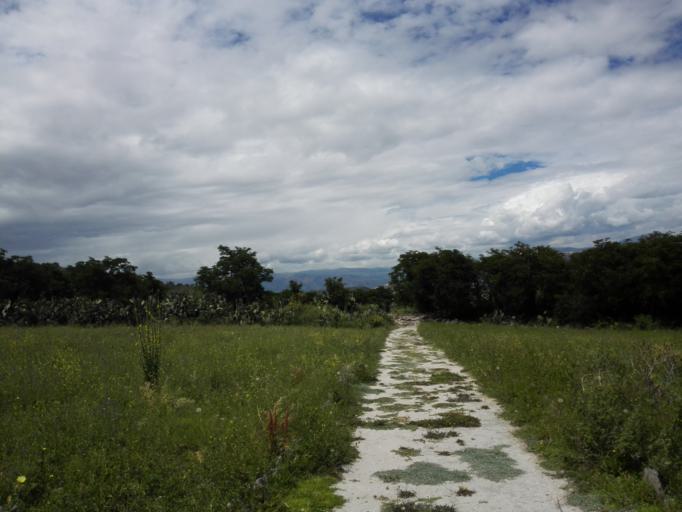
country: PE
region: Ayacucho
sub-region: Provincia de Huamanga
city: Pacaycasa
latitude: -13.0599
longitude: -74.1981
